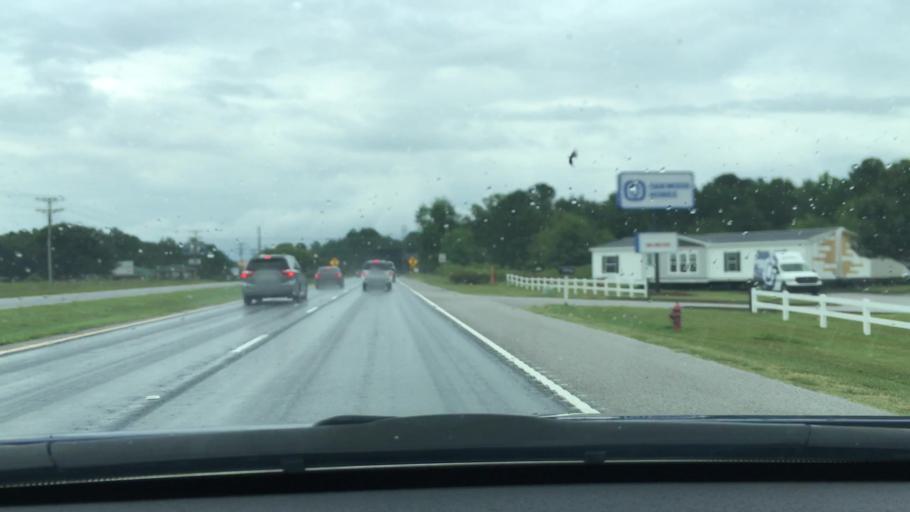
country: US
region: South Carolina
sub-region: Sumter County
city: Cherryvale
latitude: 33.9629
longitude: -80.4323
